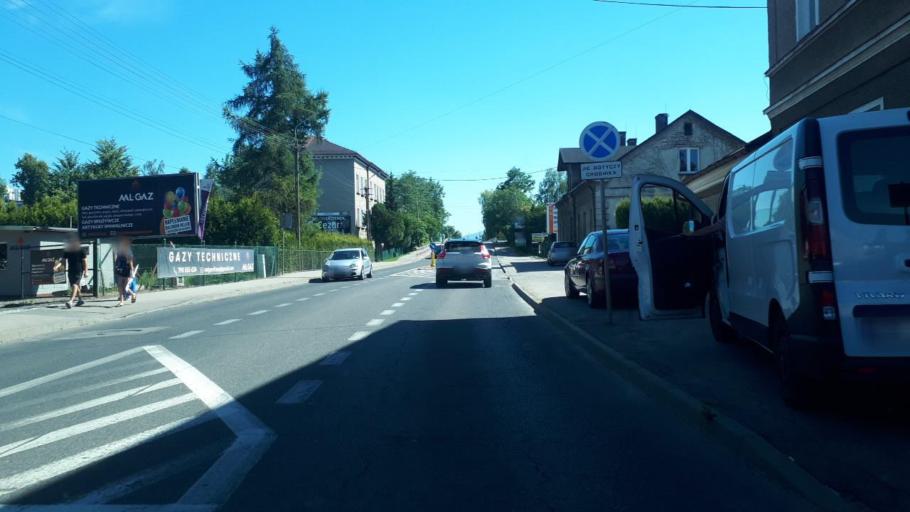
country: PL
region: Silesian Voivodeship
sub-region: Powiat bielski
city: Czechowice-Dziedzice
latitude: 49.9156
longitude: 18.9951
